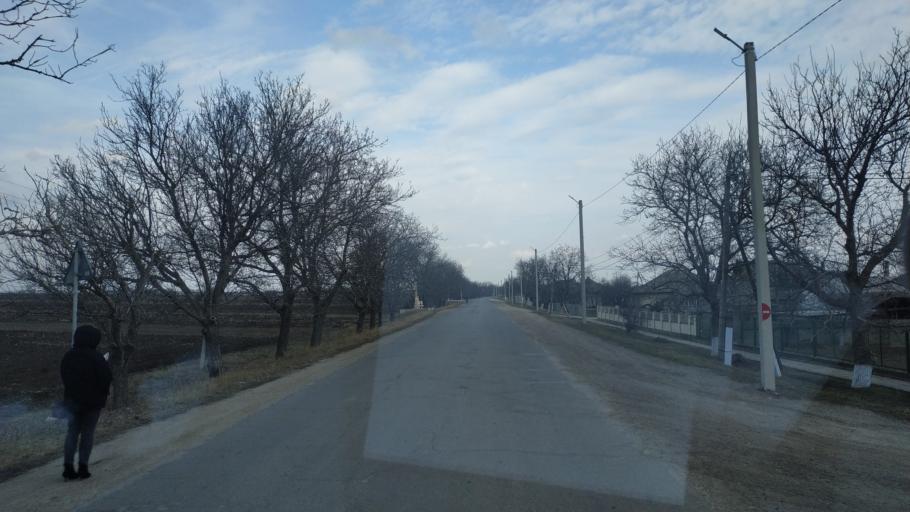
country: MD
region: Anenii Noi
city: Anenii Noi
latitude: 46.8959
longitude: 29.3057
